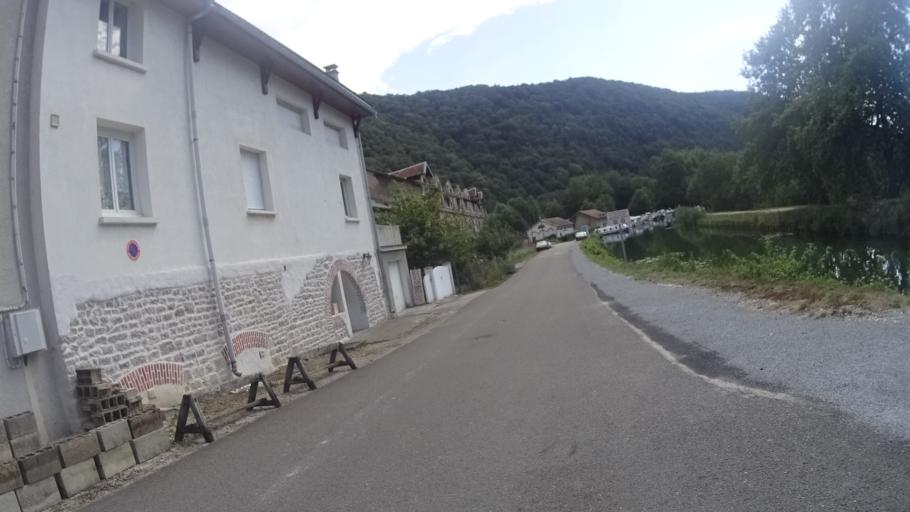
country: FR
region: Franche-Comte
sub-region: Departement du Doubs
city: Roulans
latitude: 47.2923
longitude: 6.2032
